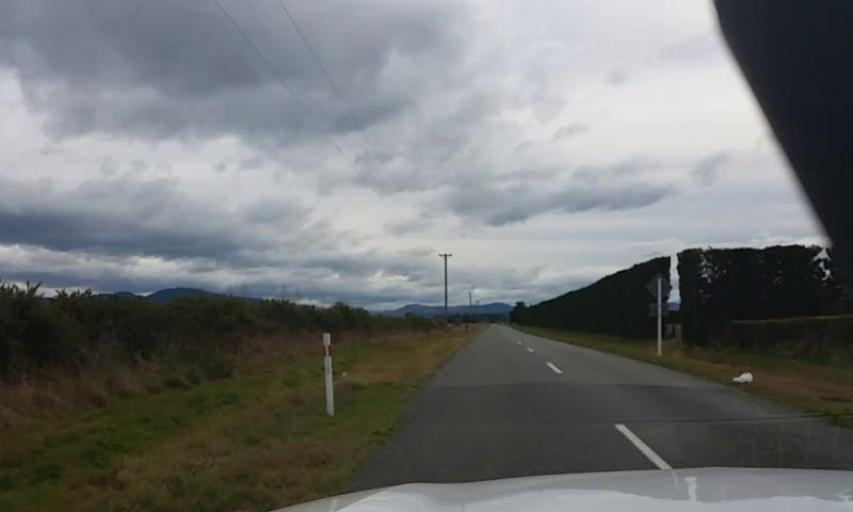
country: NZ
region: Canterbury
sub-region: Waimakariri District
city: Kaiapoi
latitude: -43.2950
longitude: 172.4376
